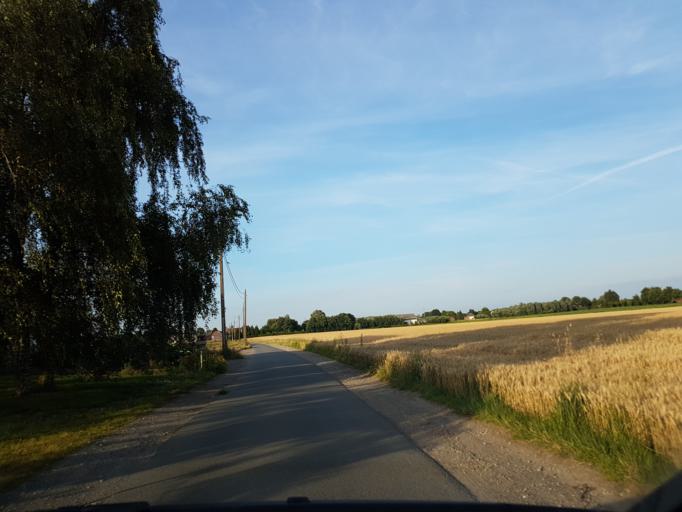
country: BE
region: Flanders
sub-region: Provincie Vlaams-Brabant
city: Opwijk
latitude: 50.9757
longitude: 4.2036
